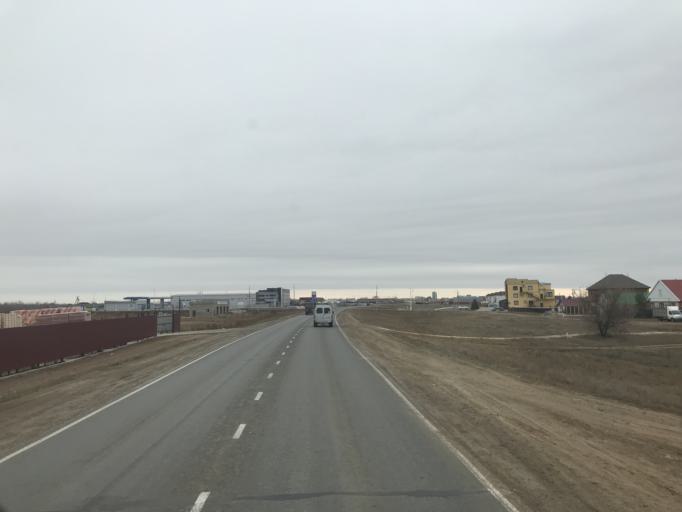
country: KZ
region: Batys Qazaqstan
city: Oral
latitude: 51.2775
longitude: 51.3957
